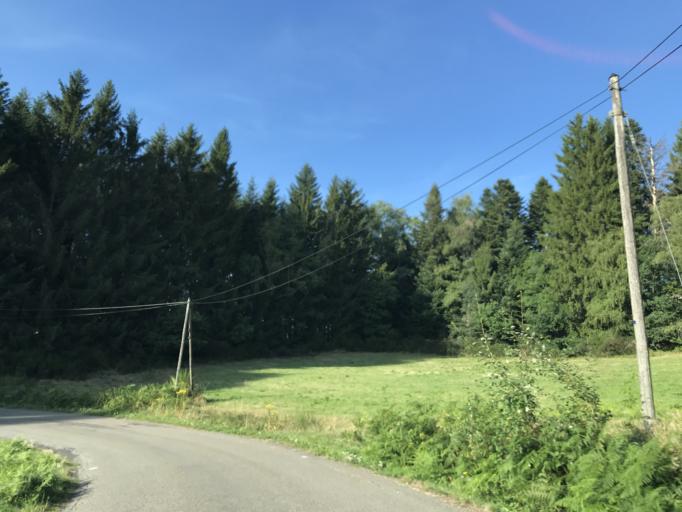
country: FR
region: Auvergne
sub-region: Departement du Puy-de-Dome
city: Job
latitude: 45.6777
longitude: 3.7317
